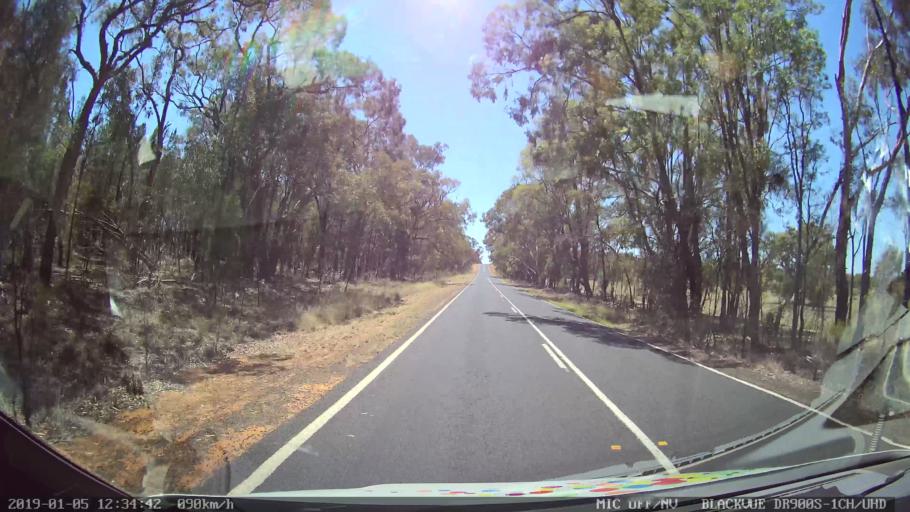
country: AU
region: New South Wales
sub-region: Warrumbungle Shire
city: Coonabarabran
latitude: -31.2115
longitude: 149.4143
